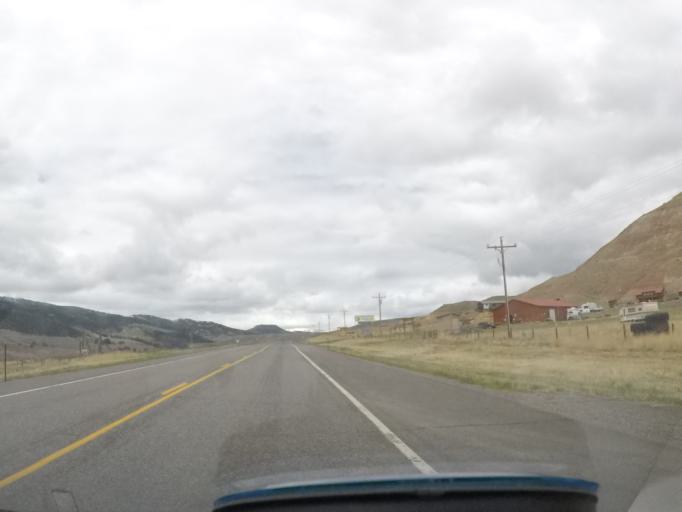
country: US
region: Wyoming
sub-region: Sublette County
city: Pinedale
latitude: 43.5711
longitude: -109.7197
